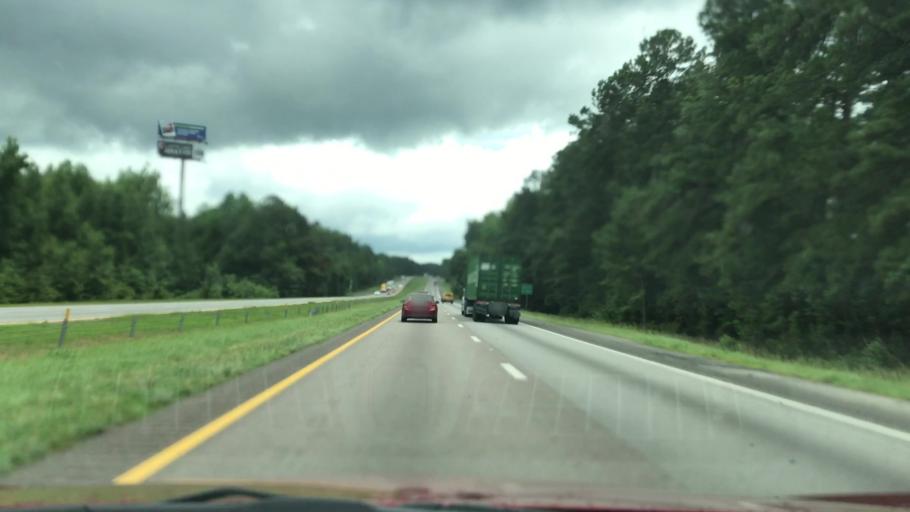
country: US
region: South Carolina
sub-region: Calhoun County
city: Saint Matthews
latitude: 33.6635
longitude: -80.8917
